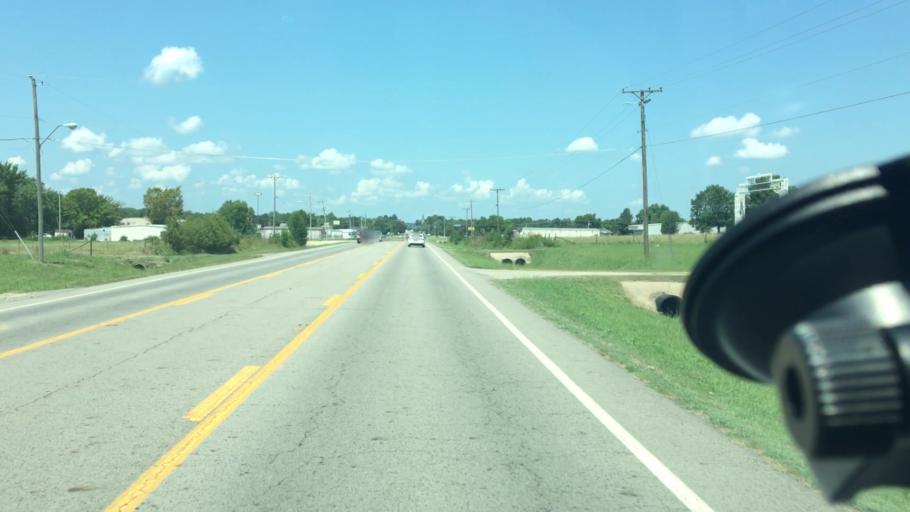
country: US
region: Arkansas
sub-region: Franklin County
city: Charleston
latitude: 35.2969
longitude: -94.0203
